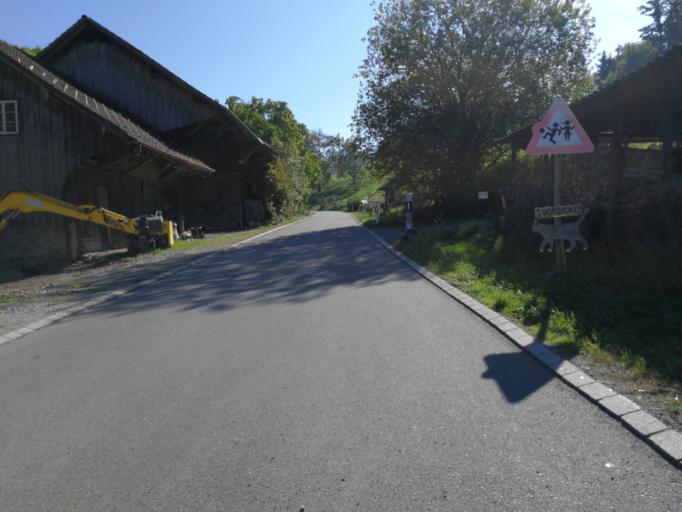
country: CH
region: Zurich
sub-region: Bezirk Uster
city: Aesch
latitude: 47.3245
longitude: 8.6676
